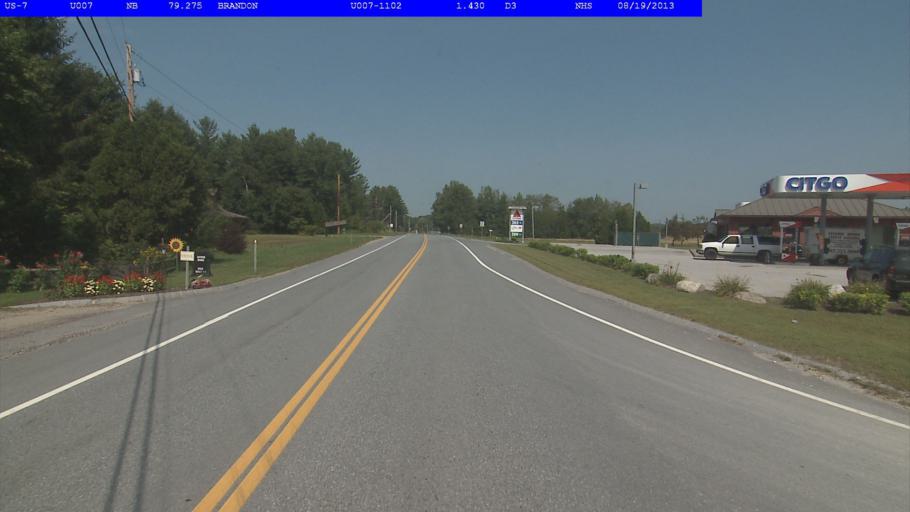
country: US
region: Vermont
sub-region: Rutland County
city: Brandon
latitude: 43.7745
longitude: -73.0534
